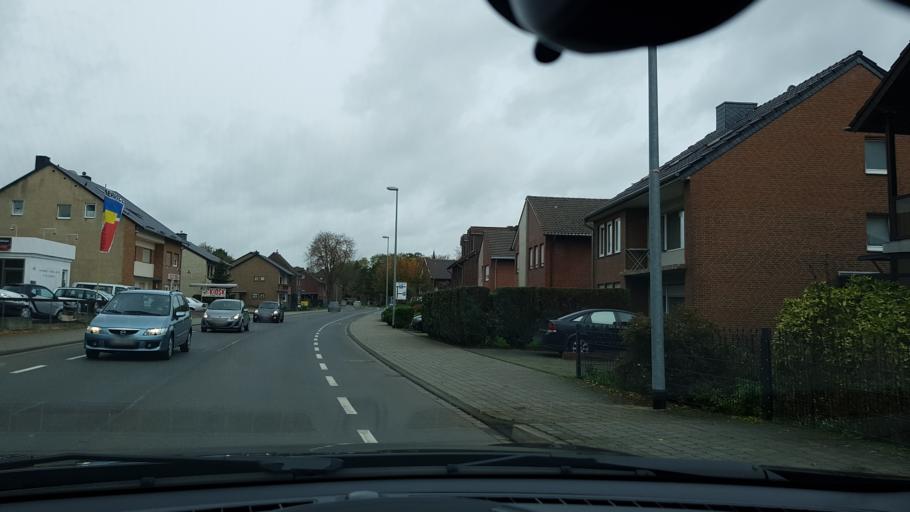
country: DE
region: North Rhine-Westphalia
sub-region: Regierungsbezirk Koln
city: Bedburg
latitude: 51.0054
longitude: 6.5589
